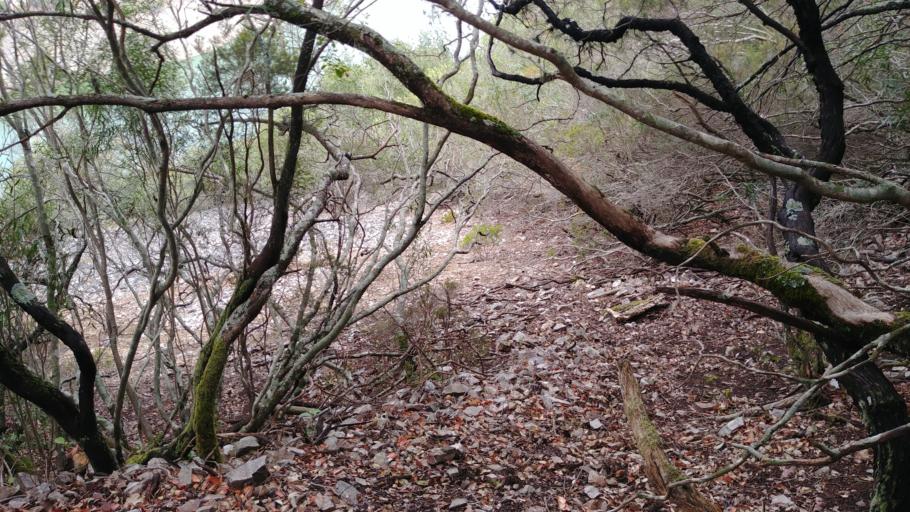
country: ES
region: Extremadura
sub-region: Provincia de Caceres
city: Torrejon el Rubio
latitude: 39.8276
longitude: -6.0316
